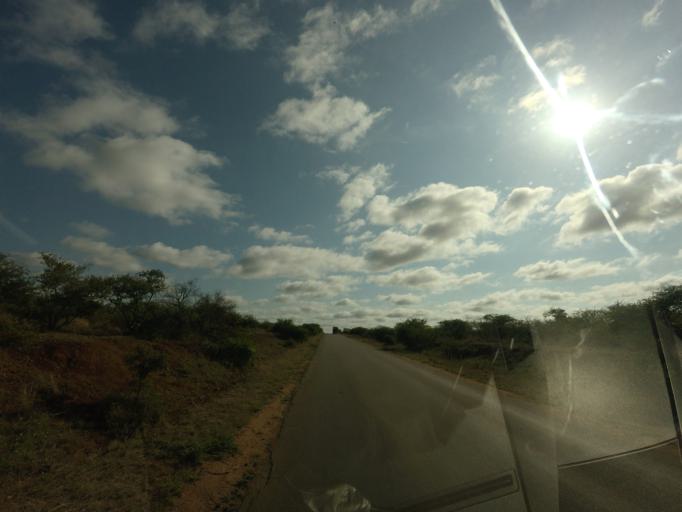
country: ZA
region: Mpumalanga
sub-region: Ehlanzeni District
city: Komatipoort
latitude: -25.1558
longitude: 31.9350
